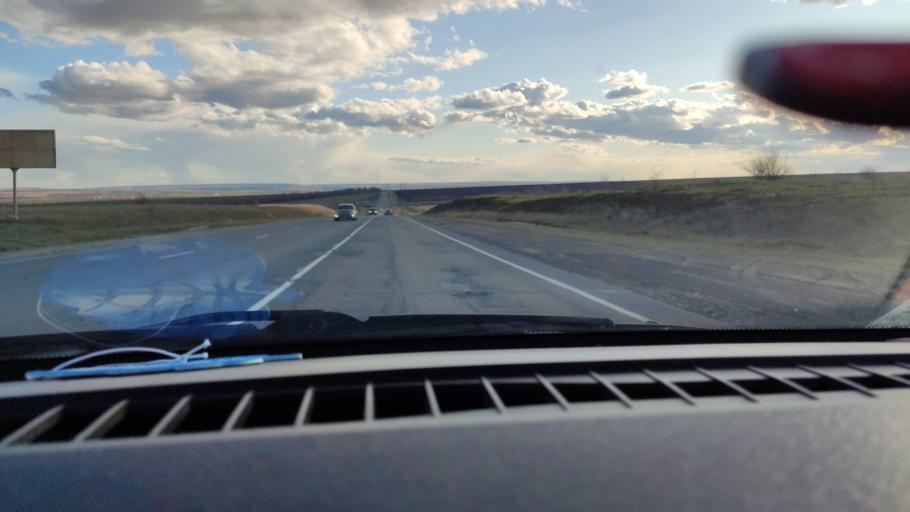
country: RU
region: Saratov
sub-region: Saratovskiy Rayon
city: Saratov
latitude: 51.7563
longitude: 46.0663
